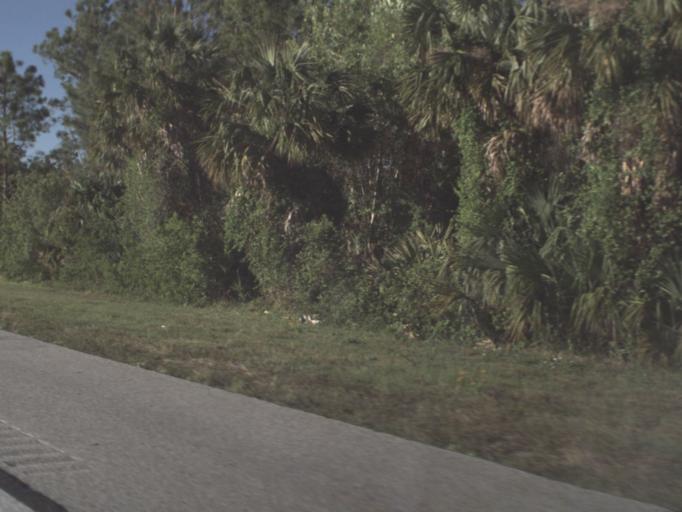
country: US
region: Florida
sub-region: Flagler County
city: Palm Coast
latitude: 29.5931
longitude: -81.2442
